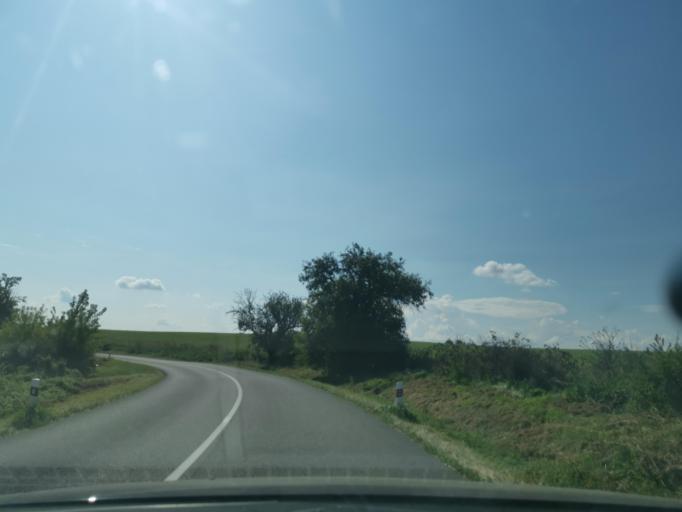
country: SK
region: Trnavsky
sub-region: Okres Senica
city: Senica
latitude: 48.6885
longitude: 17.2735
